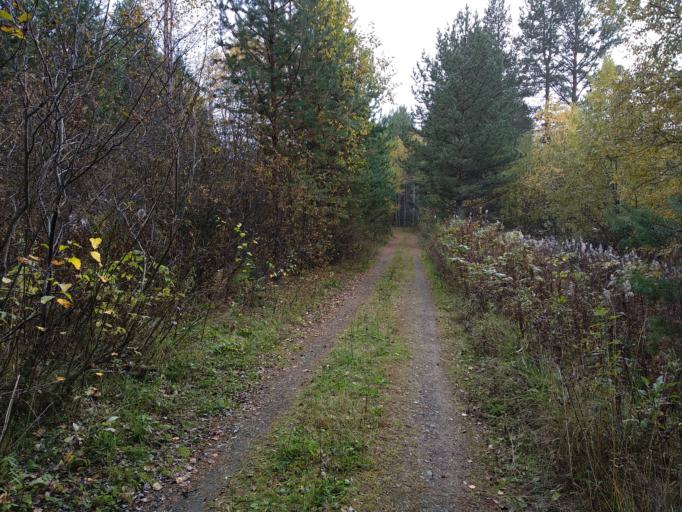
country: RU
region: Sverdlovsk
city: Krasnotur'insk
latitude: 59.7935
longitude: 60.1345
